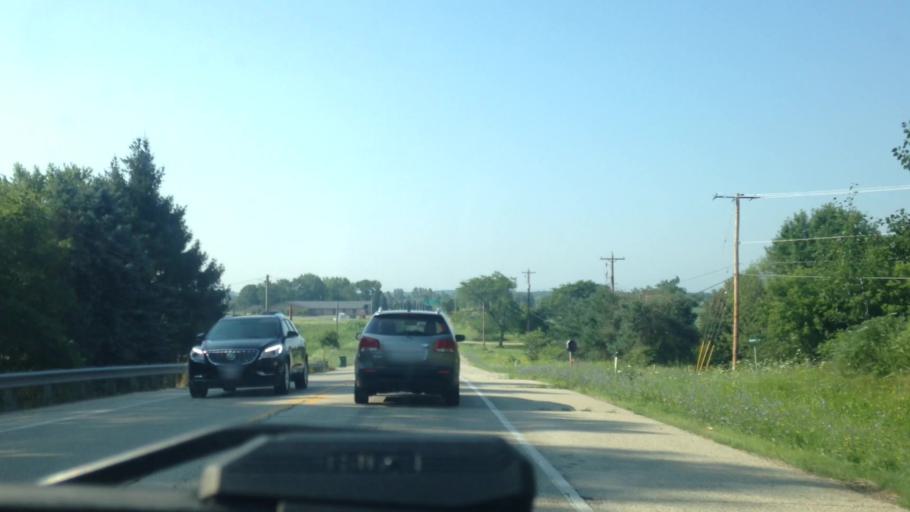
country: US
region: Wisconsin
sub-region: Waukesha County
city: Merton
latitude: 43.1987
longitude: -88.2615
